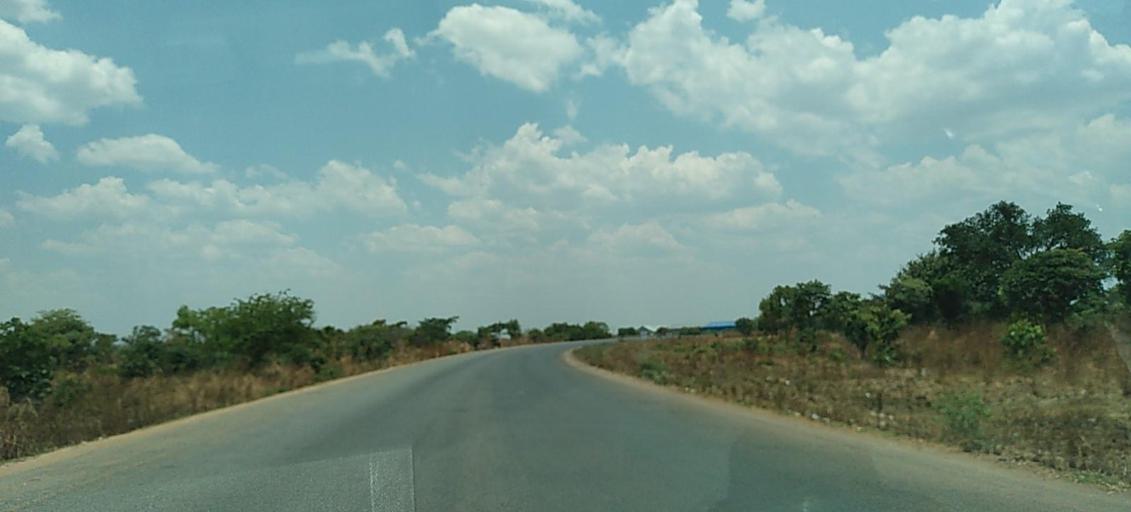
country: ZM
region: Central
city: Kapiri Mposhi
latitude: -13.8932
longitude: 28.6618
